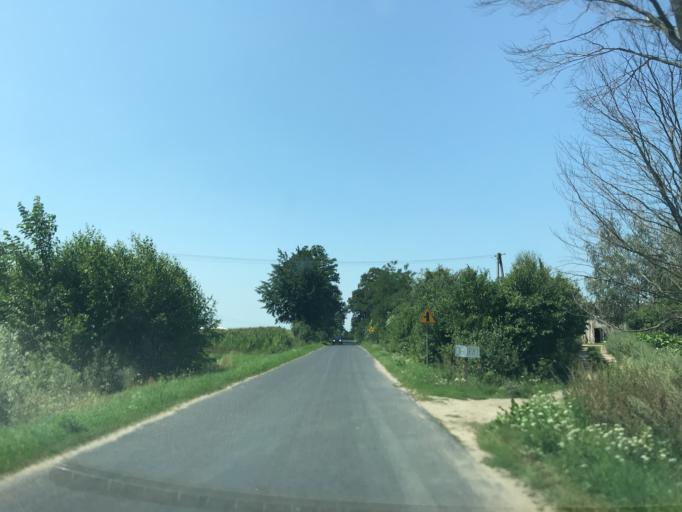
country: PL
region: Kujawsko-Pomorskie
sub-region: Powiat lipnowski
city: Chrostkowo
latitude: 52.9898
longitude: 19.2493
